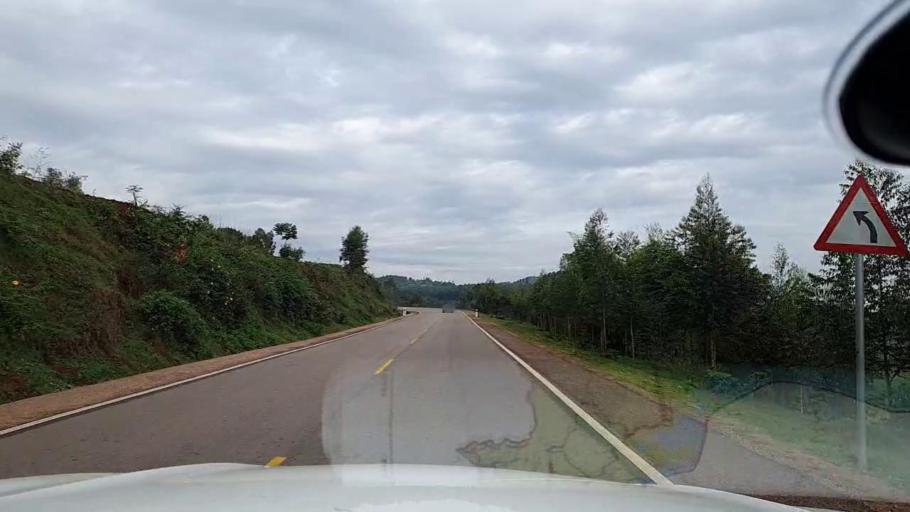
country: RW
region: Southern Province
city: Butare
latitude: -2.5597
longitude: 29.7184
